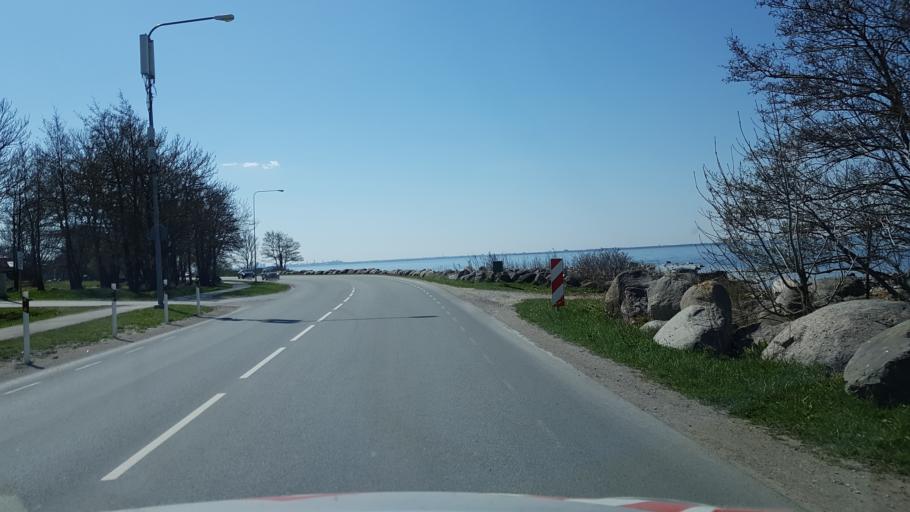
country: EE
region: Harju
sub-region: Viimsi vald
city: Rummu
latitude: 59.5367
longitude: 24.7934
